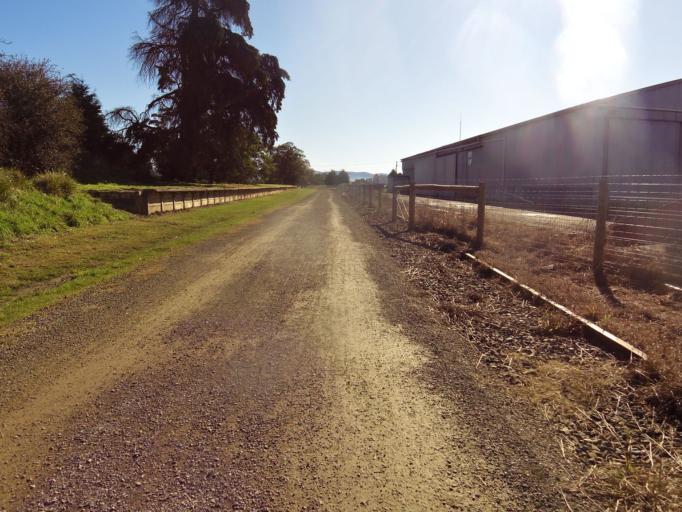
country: AU
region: Victoria
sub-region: Yarra Ranges
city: Lilydale
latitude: -37.7268
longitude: 145.3717
